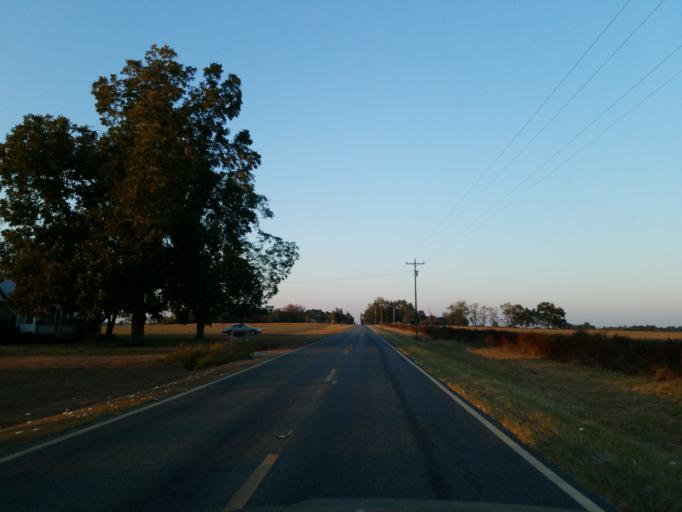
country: US
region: Georgia
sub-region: Ben Hill County
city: Fitzgerald
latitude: 31.6738
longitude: -83.3856
